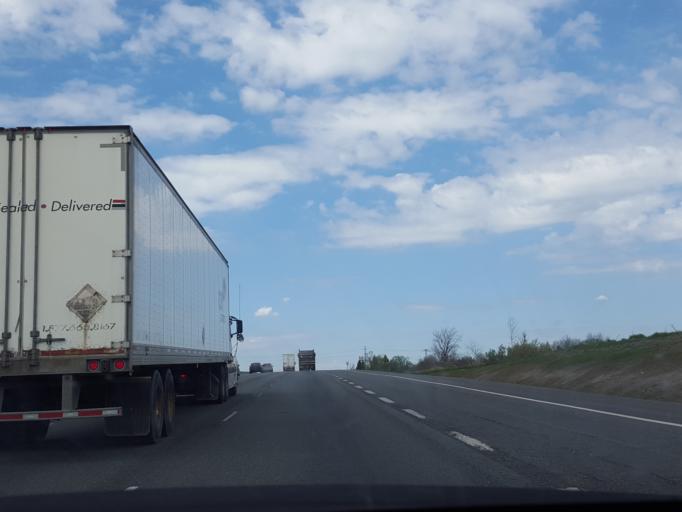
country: CA
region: Ontario
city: Oshawa
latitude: 43.8836
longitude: -78.7268
